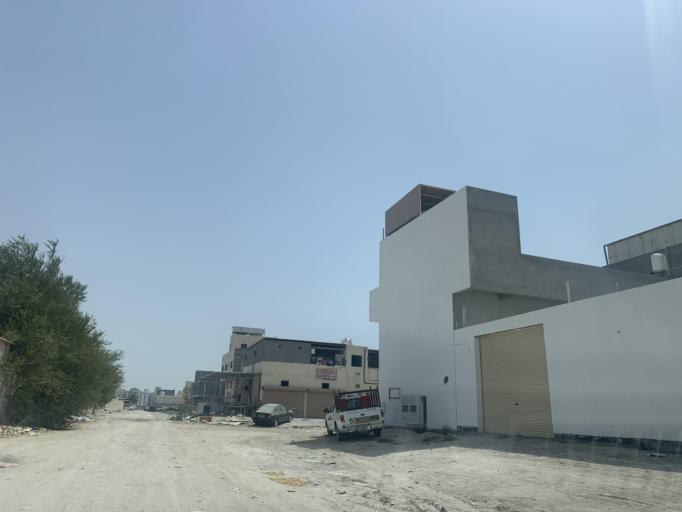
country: BH
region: Central Governorate
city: Madinat Hamad
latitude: 26.1432
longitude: 50.4872
